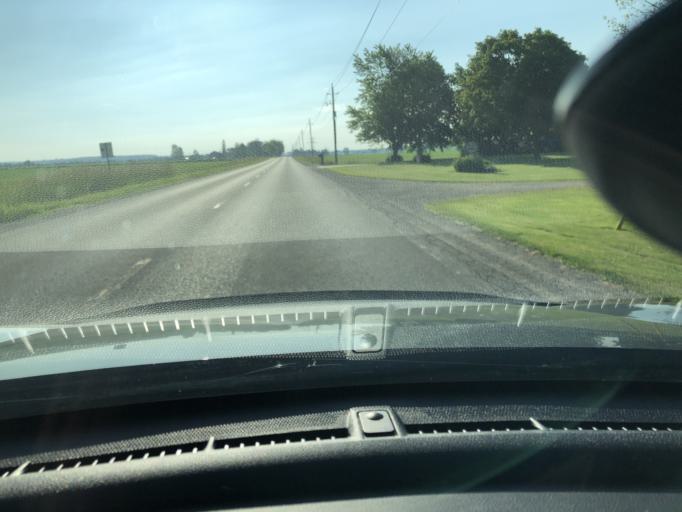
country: CA
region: Ontario
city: Stratford
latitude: 43.3892
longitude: -80.9514
